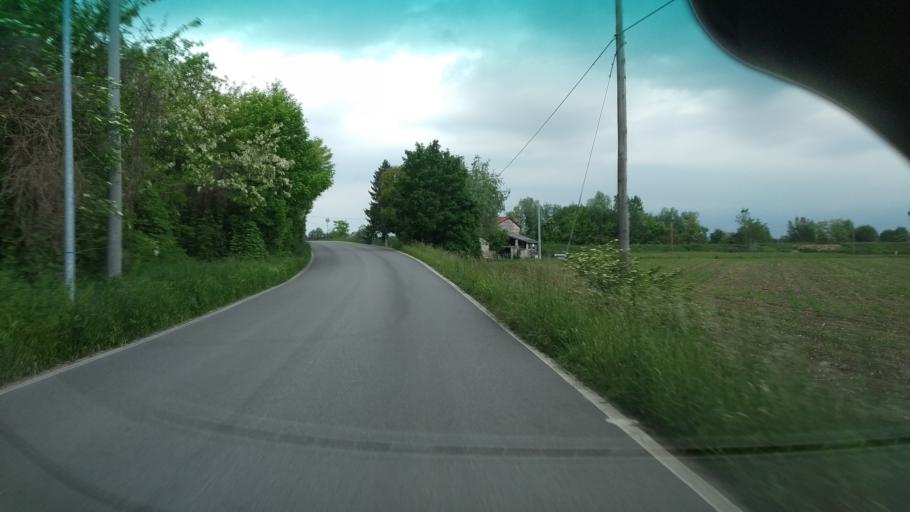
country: IT
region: Veneto
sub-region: Provincia di Vicenza
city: Poianella
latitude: 45.6380
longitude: 11.6159
